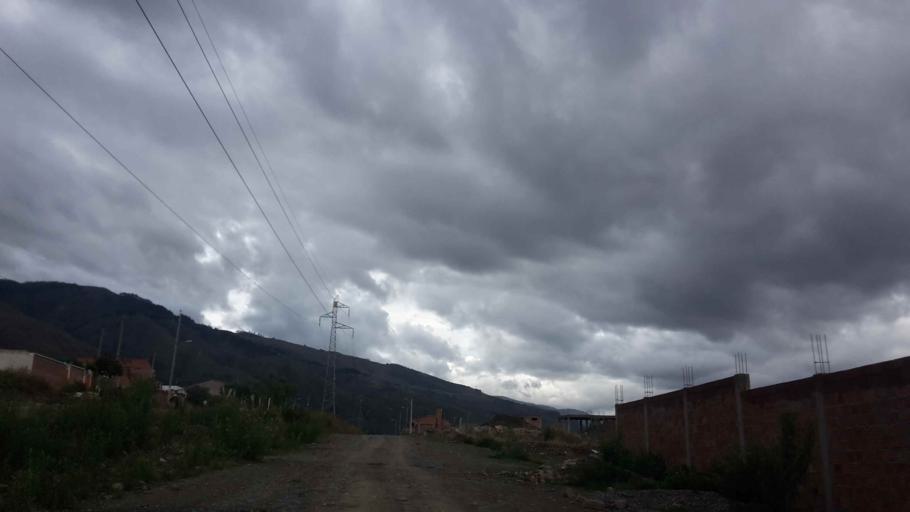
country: BO
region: Cochabamba
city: Cochabamba
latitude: -17.3785
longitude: -66.0641
